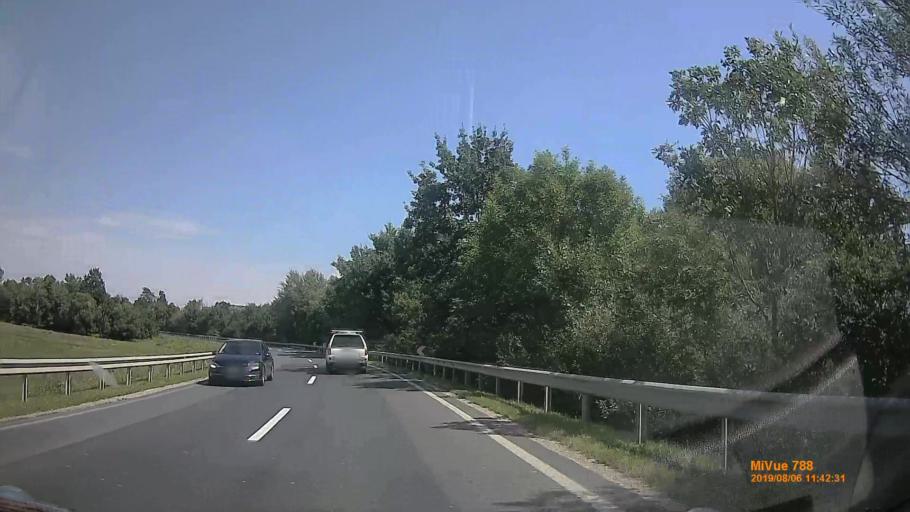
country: HU
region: Vas
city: Kormend
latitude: 46.9984
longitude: 16.5440
